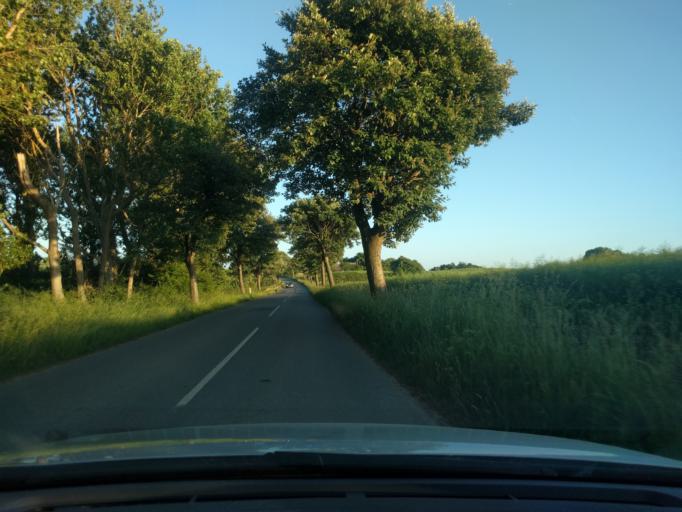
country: DK
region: South Denmark
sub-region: Kerteminde Kommune
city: Kerteminde
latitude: 55.5884
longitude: 10.6306
